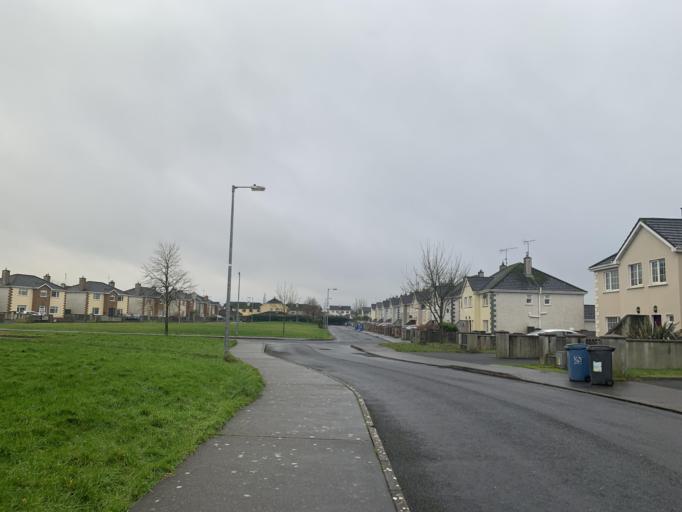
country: IE
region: Connaught
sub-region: County Galway
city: Tuam
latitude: 53.5270
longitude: -8.8552
